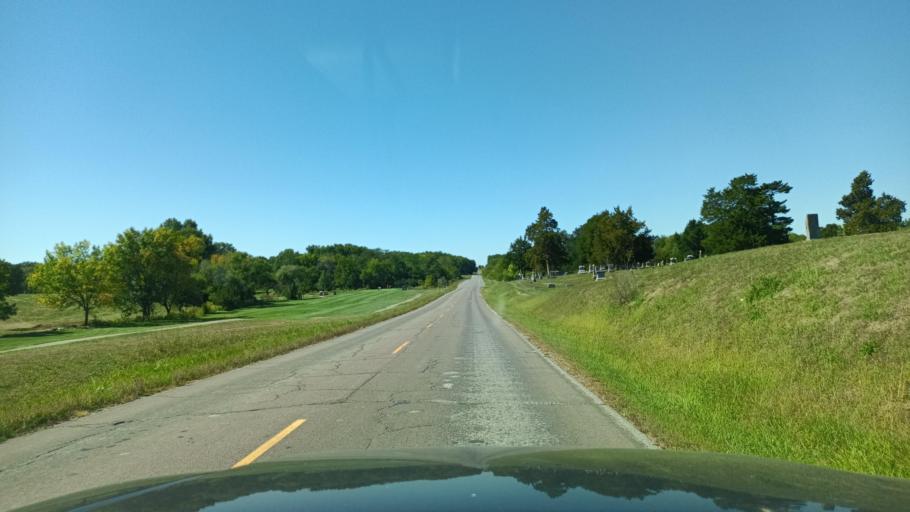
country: US
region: Missouri
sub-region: Macon County
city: La Plata
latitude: 40.0211
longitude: -92.4986
